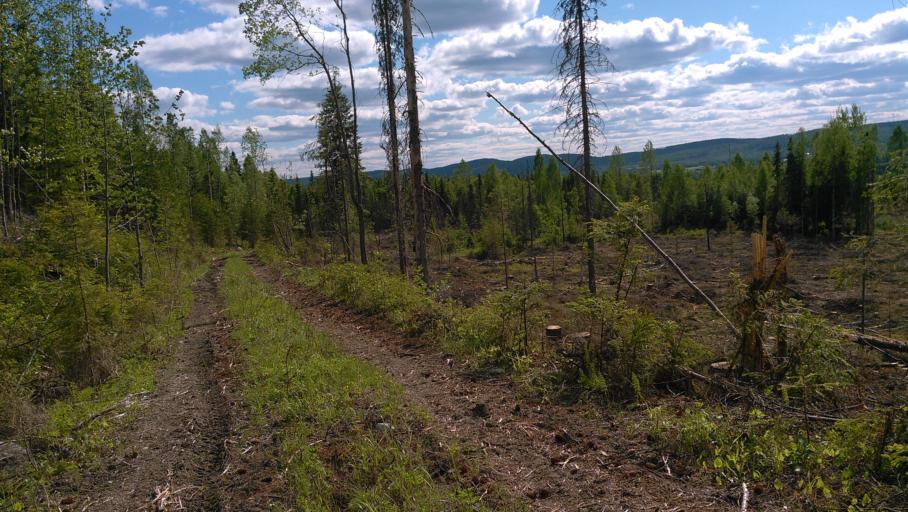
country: SE
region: Vaesterbotten
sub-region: Vannas Kommun
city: Vannasby
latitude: 63.9296
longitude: 19.8916
